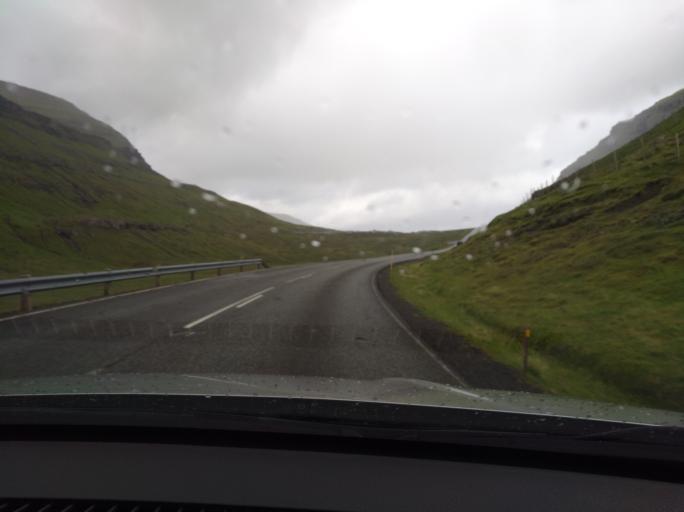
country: FO
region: Eysturoy
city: Fuglafjordur
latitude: 62.2325
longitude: -6.8806
